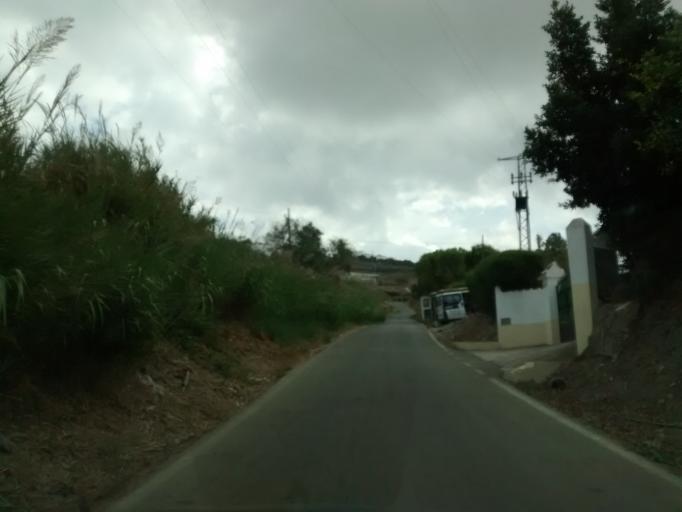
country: ES
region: Andalusia
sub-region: Provincia de Cadiz
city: Medina Sidonia
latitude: 36.4579
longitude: -5.9360
